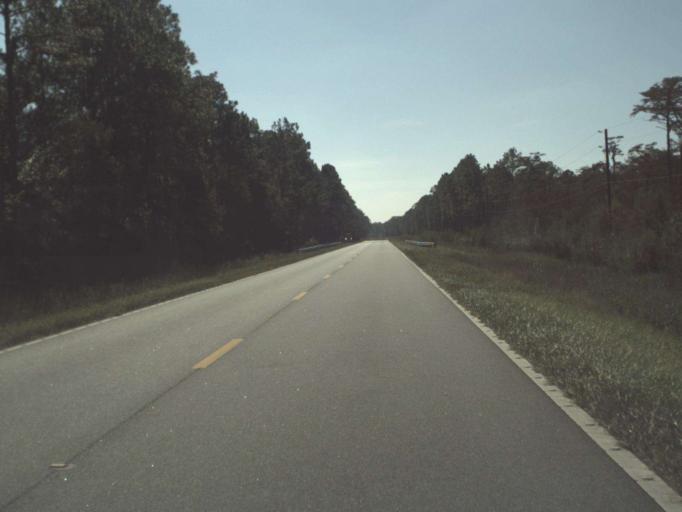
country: US
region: Florida
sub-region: Liberty County
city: Bristol
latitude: 30.2848
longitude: -84.8399
